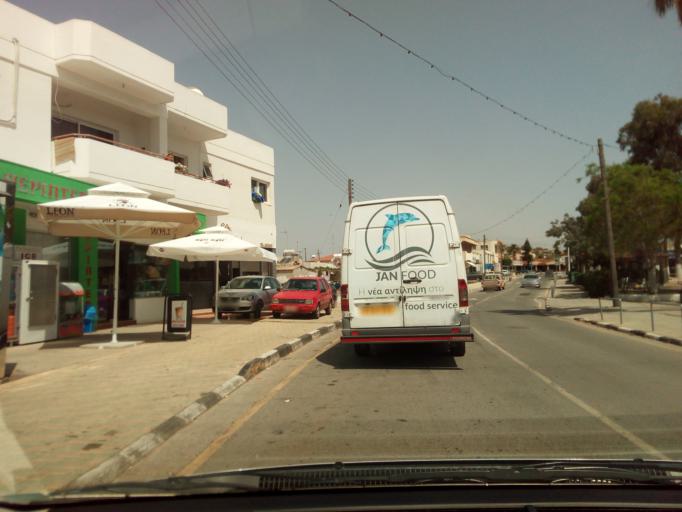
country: CY
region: Larnaka
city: Xylotymbou
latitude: 34.9909
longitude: 33.7788
